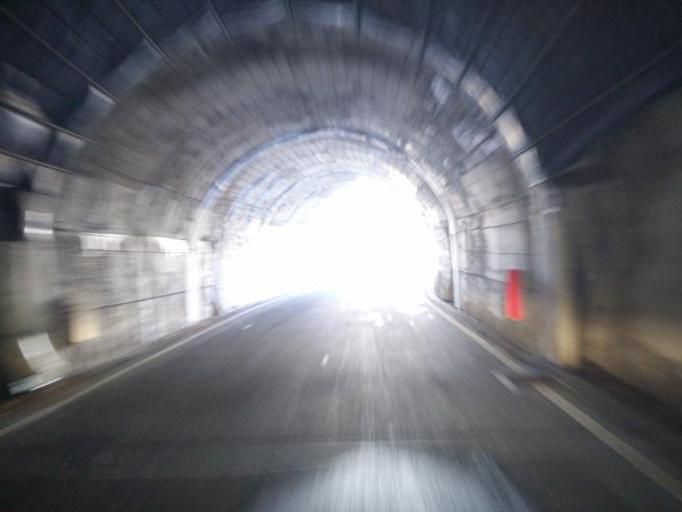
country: IT
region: Trentino-Alto Adige
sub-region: Bolzano
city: Moso in Passiria
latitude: 46.8781
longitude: 11.1582
